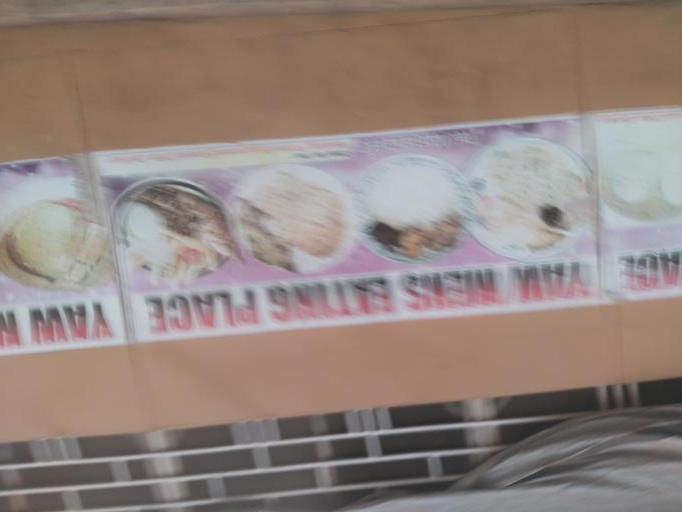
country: GH
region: Ashanti
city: Tafo
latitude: 6.7095
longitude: -1.6081
